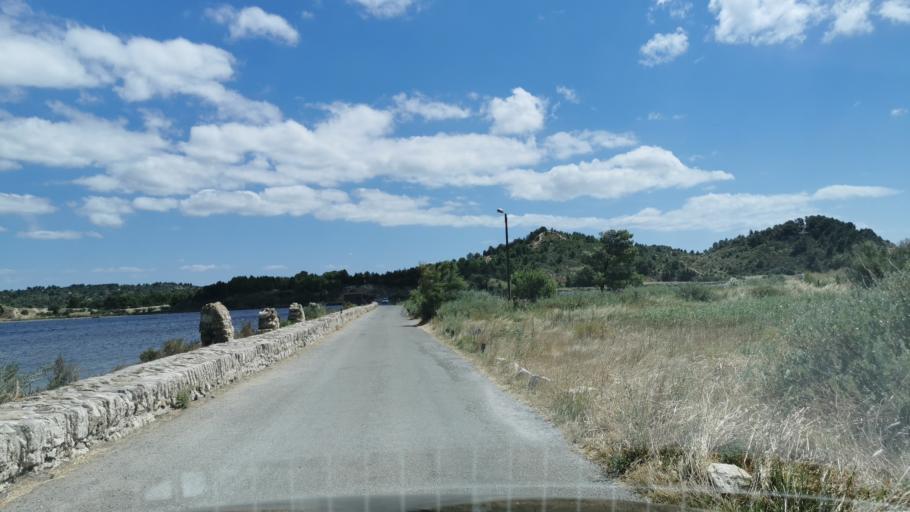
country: FR
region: Languedoc-Roussillon
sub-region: Departement de l'Aude
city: Peyriac-de-Mer
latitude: 43.0847
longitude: 2.9633
